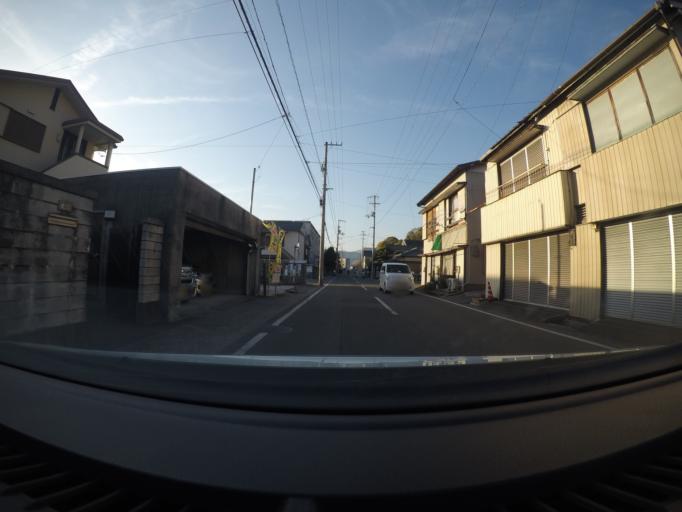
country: JP
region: Kochi
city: Kochi-shi
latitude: 33.5472
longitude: 133.5694
